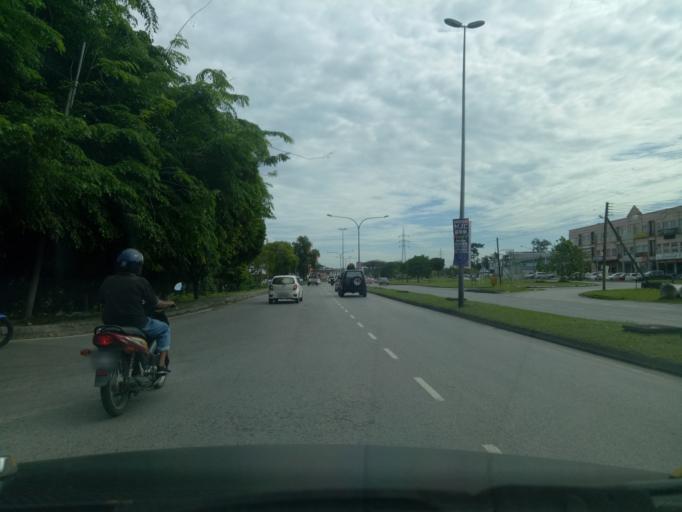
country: MY
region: Sarawak
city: Kuching
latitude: 1.4882
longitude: 110.3307
